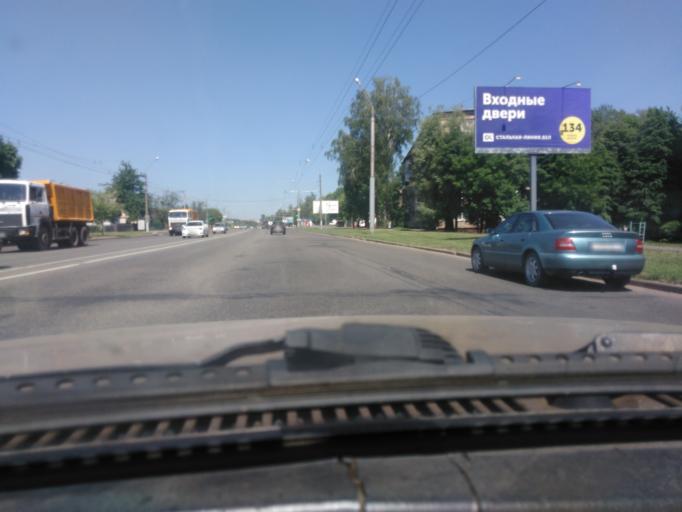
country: BY
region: Mogilev
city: Mahilyow
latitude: 53.9356
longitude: 30.3533
